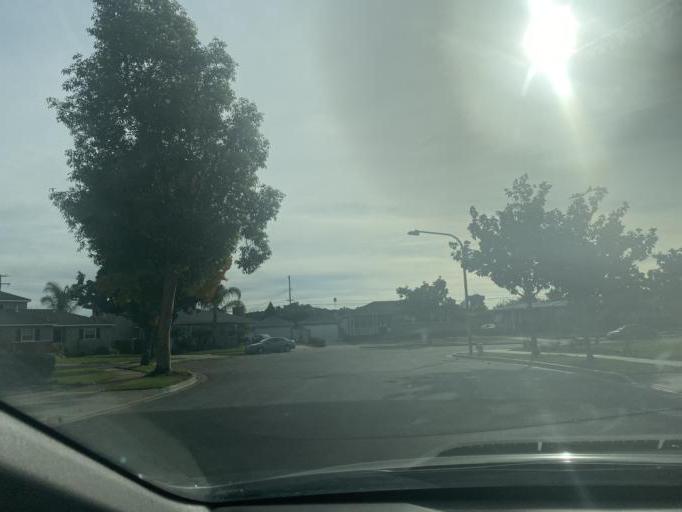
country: US
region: California
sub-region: Orange County
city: Brea
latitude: 33.9077
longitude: -117.8962
